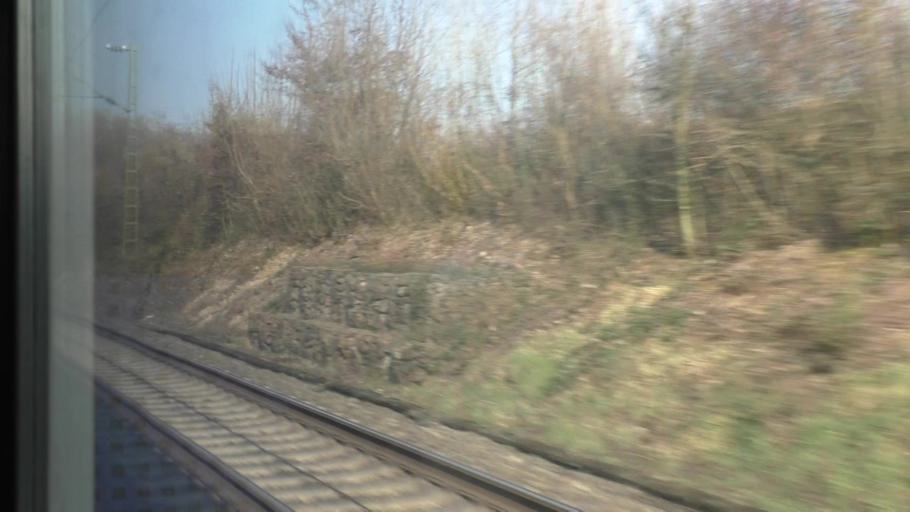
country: DE
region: Baden-Wuerttemberg
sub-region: Freiburg Region
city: Unterkrozingen
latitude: 47.9117
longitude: 7.6863
